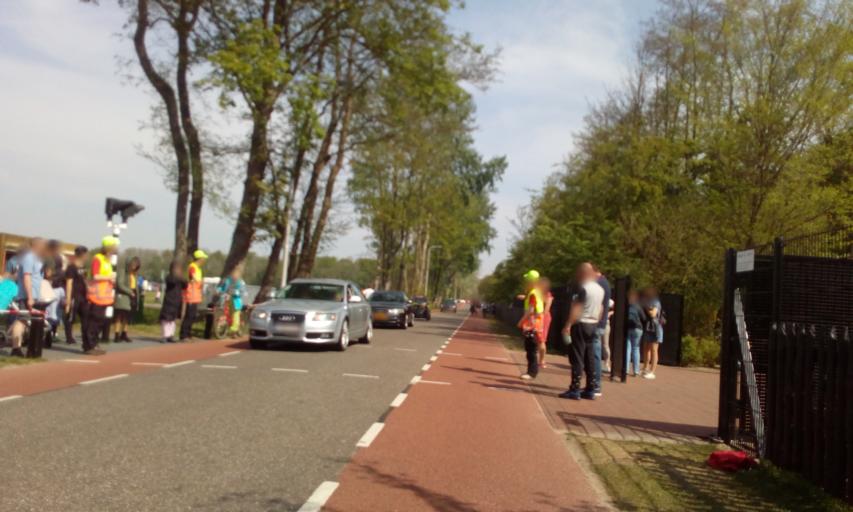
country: NL
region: South Holland
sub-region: Gemeente Lisse
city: Lisse
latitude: 52.2718
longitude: 4.5442
